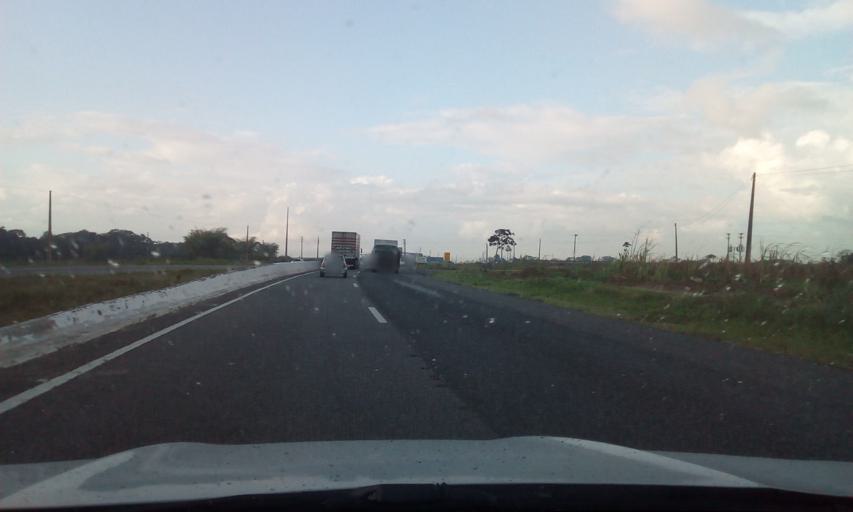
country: BR
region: Pernambuco
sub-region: Goiana
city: Goiana
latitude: -7.5122
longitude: -34.9885
